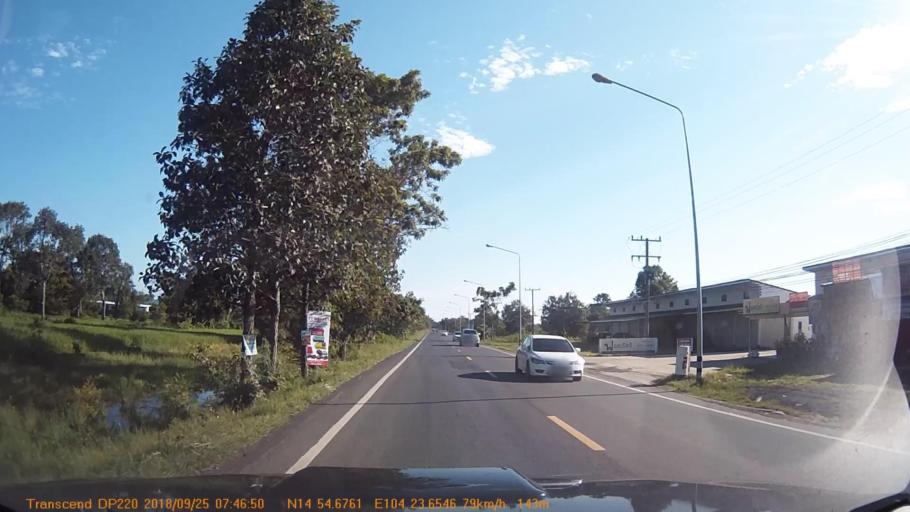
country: TH
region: Sisaket
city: Phayu
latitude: 14.9114
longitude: 104.3943
